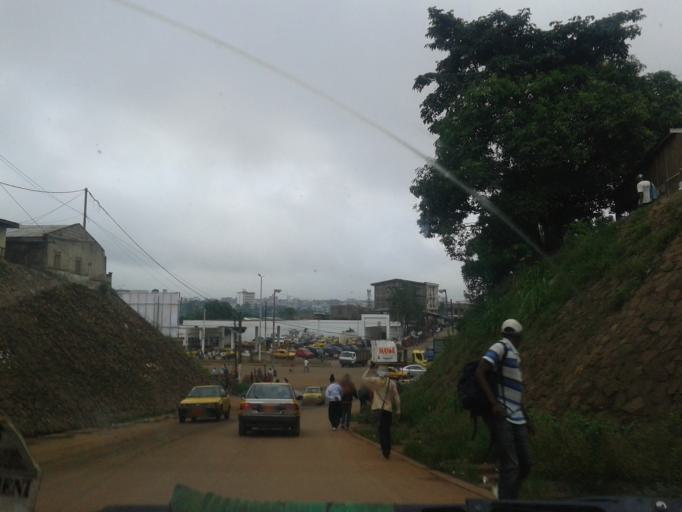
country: CM
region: Centre
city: Yaounde
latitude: 3.8877
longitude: 11.5303
